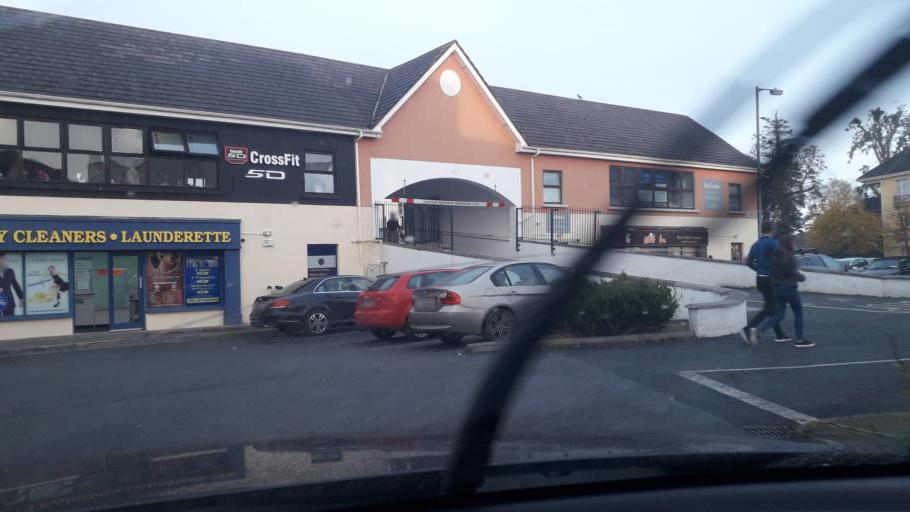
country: IE
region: Leinster
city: Hartstown
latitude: 53.3949
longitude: -6.4405
